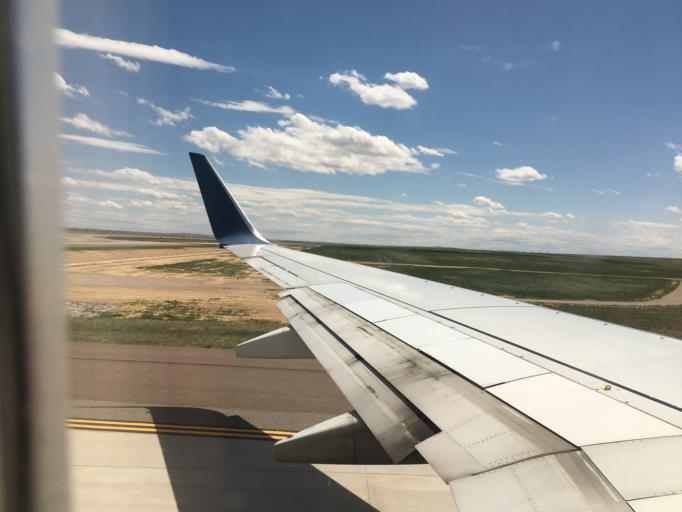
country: US
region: Colorado
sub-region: Weld County
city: Lochbuie
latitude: 39.8567
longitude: -104.6450
